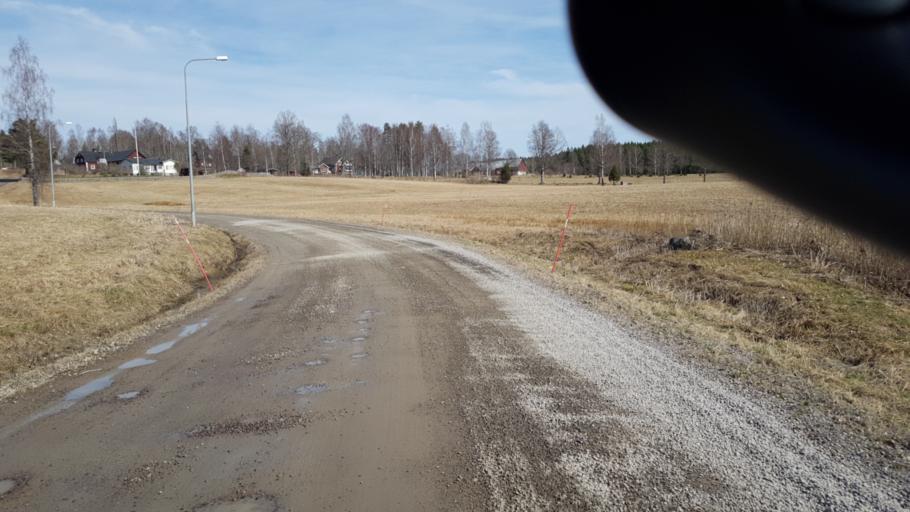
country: SE
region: Vaermland
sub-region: Arvika Kommun
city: Arvika
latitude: 59.5271
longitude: 12.8303
